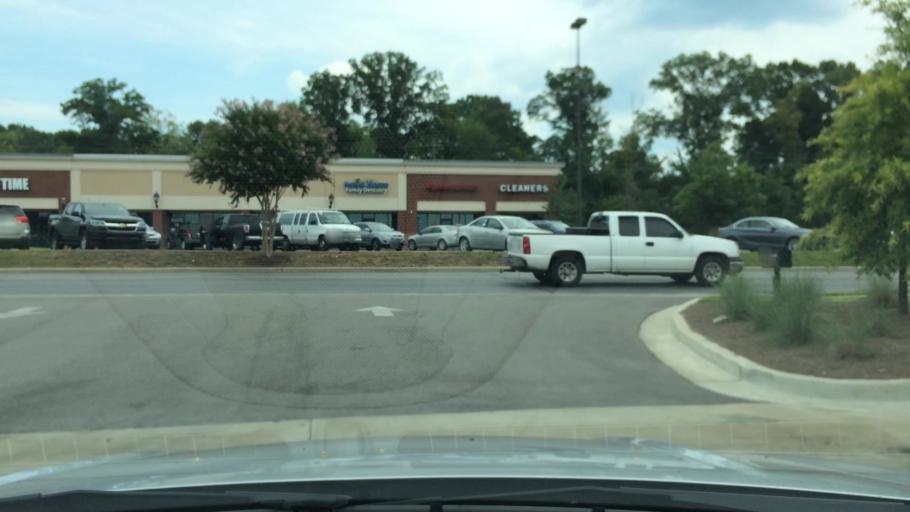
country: US
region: Tennessee
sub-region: Maury County
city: Spring Hill
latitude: 35.7400
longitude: -86.8926
